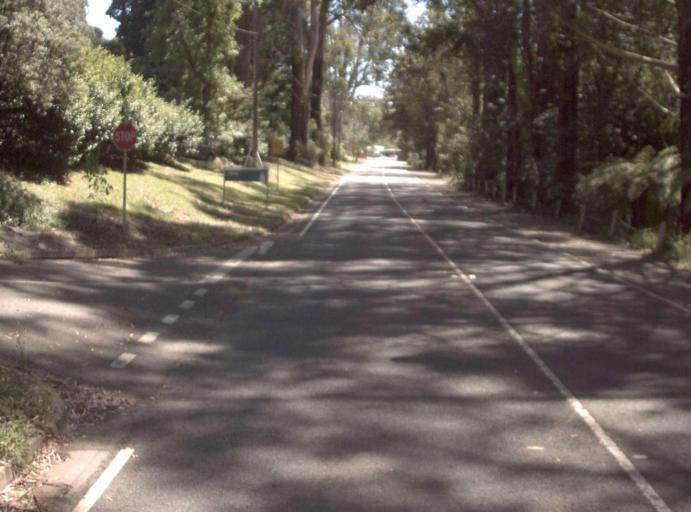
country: AU
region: Victoria
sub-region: Yarra Ranges
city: Olinda
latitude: -37.8575
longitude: 145.3675
